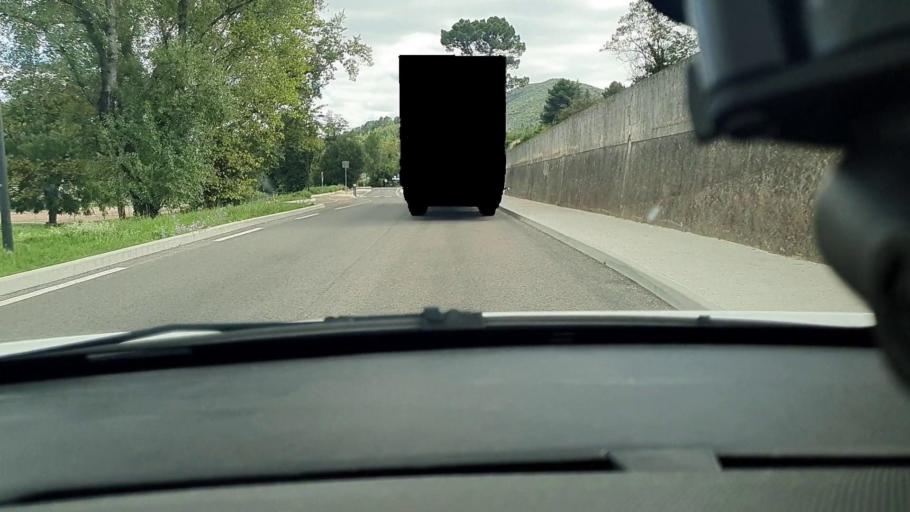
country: FR
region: Languedoc-Roussillon
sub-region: Departement du Gard
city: Saint-Florent-sur-Auzonnet
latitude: 44.2495
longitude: 4.0885
